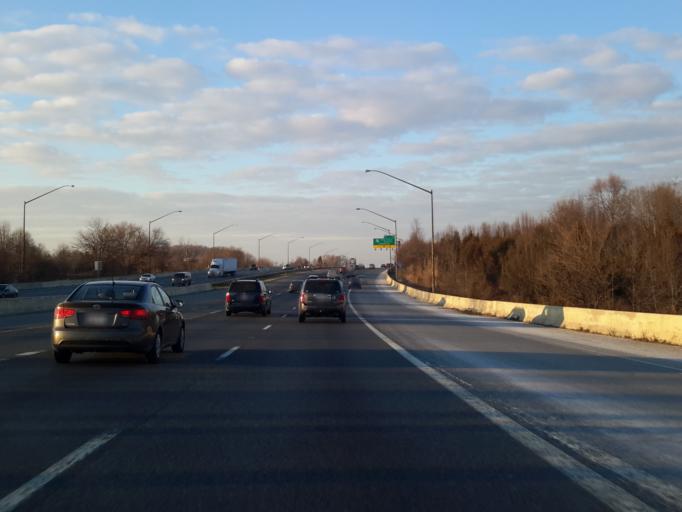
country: US
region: Maryland
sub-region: Montgomery County
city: Germantown
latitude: 39.1878
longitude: -77.2574
